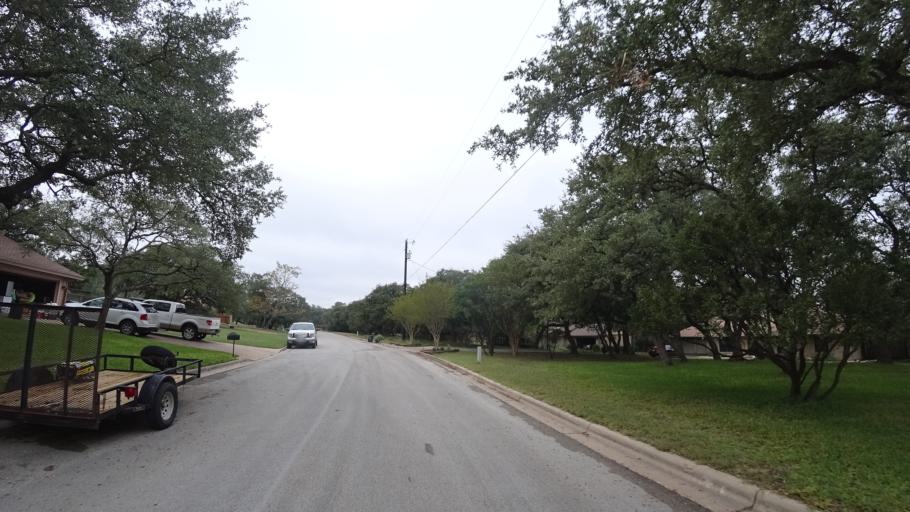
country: US
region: Texas
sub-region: Travis County
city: Shady Hollow
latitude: 30.2224
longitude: -97.9058
